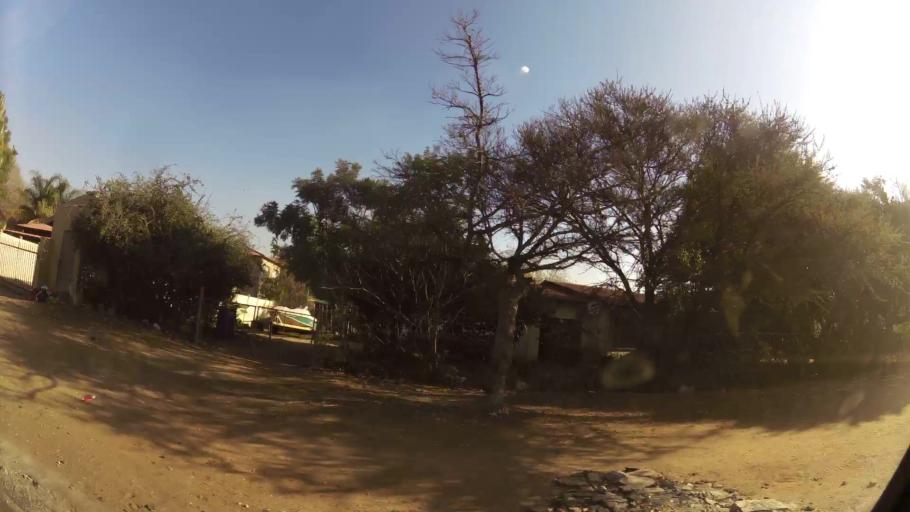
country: ZA
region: North-West
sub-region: Bojanala Platinum District Municipality
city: Rustenburg
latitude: -25.6583
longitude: 27.2587
